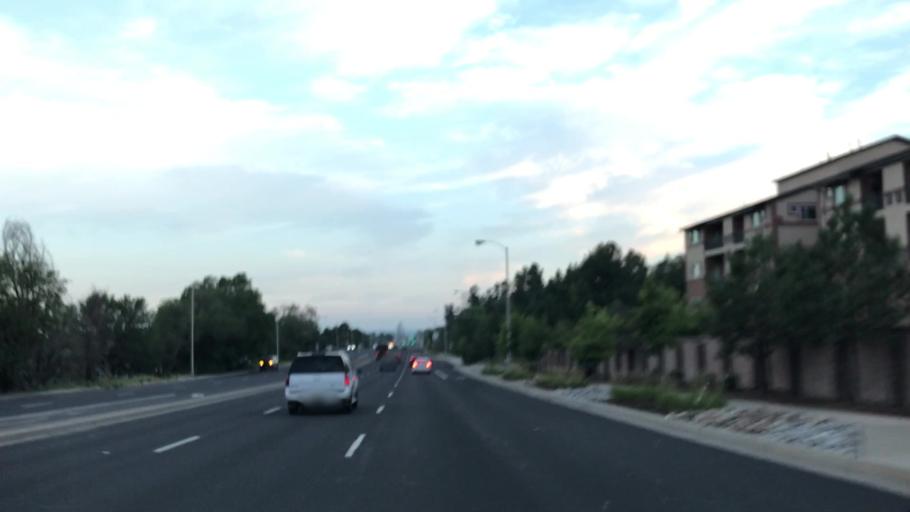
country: US
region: Colorado
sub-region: El Paso County
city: Cimarron Hills
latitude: 38.8737
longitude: -104.7572
